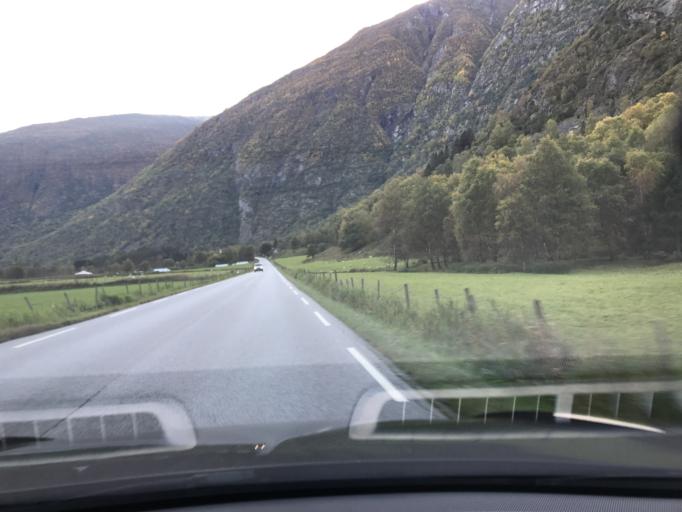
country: NO
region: Sogn og Fjordane
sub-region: Laerdal
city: Laerdalsoyri
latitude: 61.0811
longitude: 7.5064
